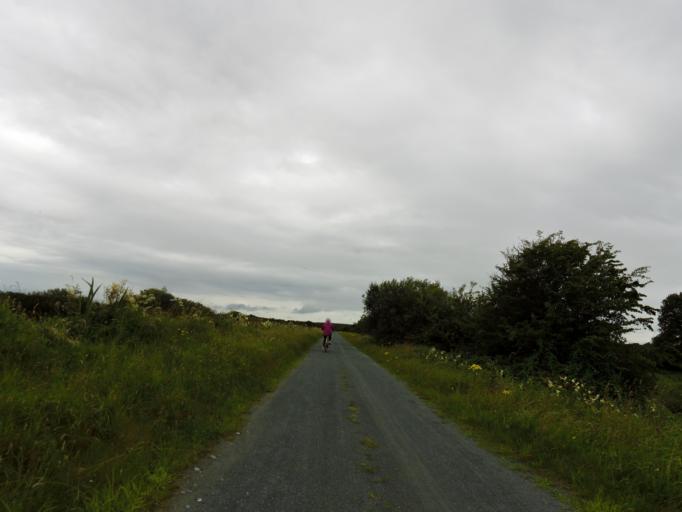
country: IE
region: Leinster
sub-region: An Iarmhi
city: Moate
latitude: 53.5803
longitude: -7.6012
